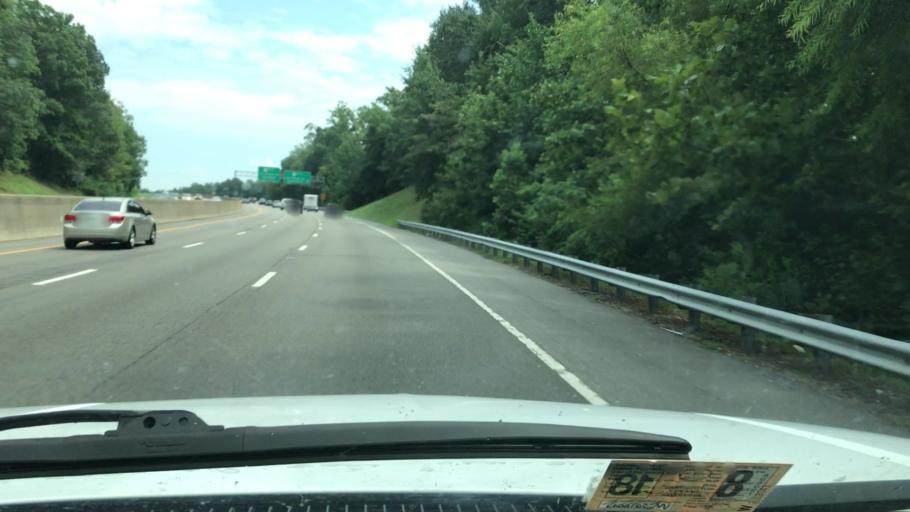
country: US
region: Virginia
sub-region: Chesterfield County
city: Bensley
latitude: 37.4534
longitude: -77.4923
